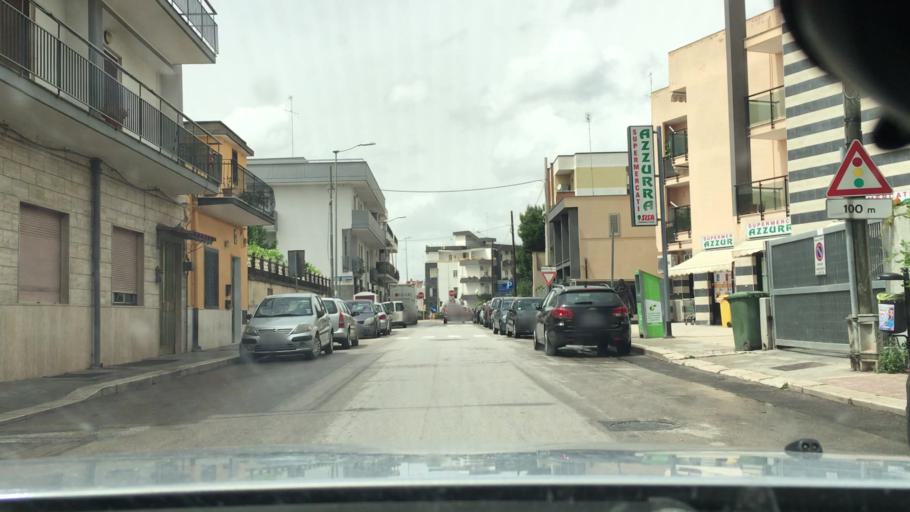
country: IT
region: Apulia
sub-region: Provincia di Bari
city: Capurso
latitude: 41.0504
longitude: 16.9189
